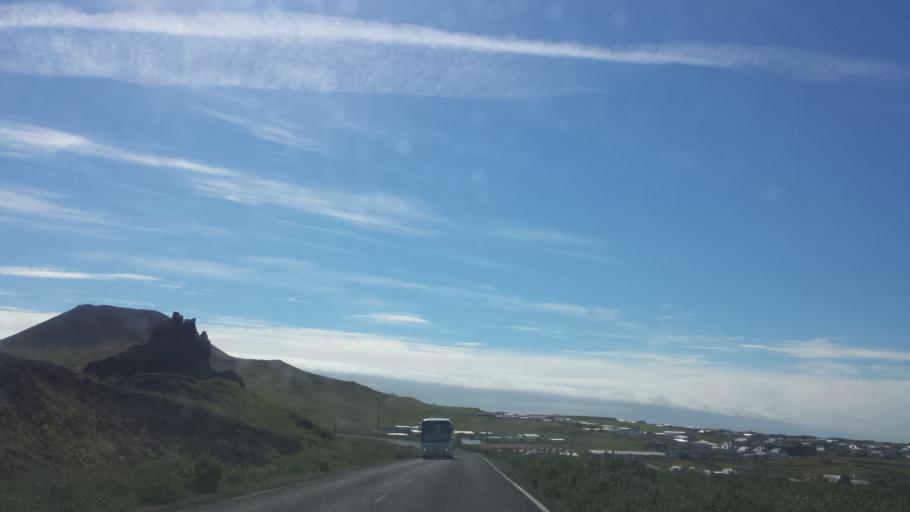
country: IS
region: South
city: Vestmannaeyjar
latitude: 63.4405
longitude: -20.2558
